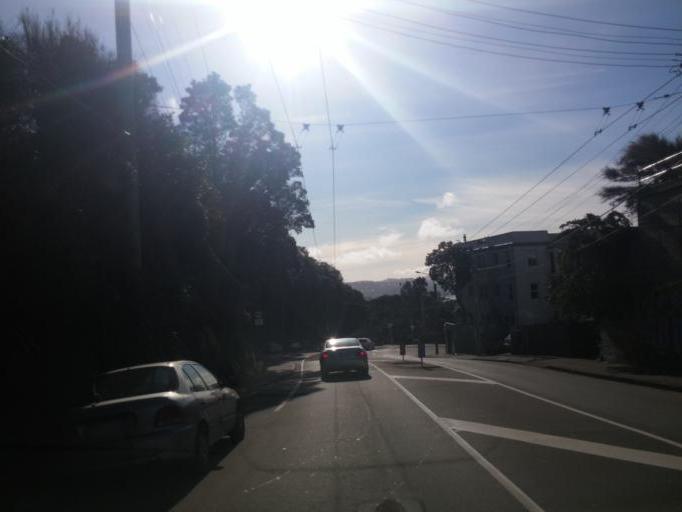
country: NZ
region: Wellington
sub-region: Wellington City
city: Brooklyn
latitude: -41.3034
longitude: 174.7638
